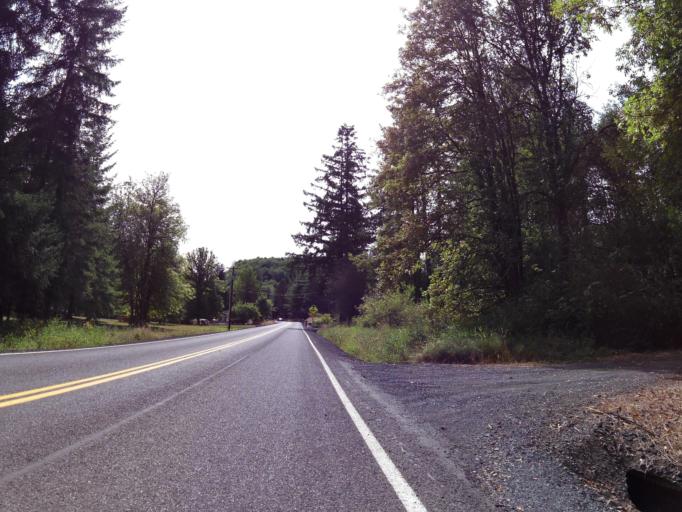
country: US
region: Washington
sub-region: Lewis County
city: Napavine
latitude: 46.5643
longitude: -122.9657
